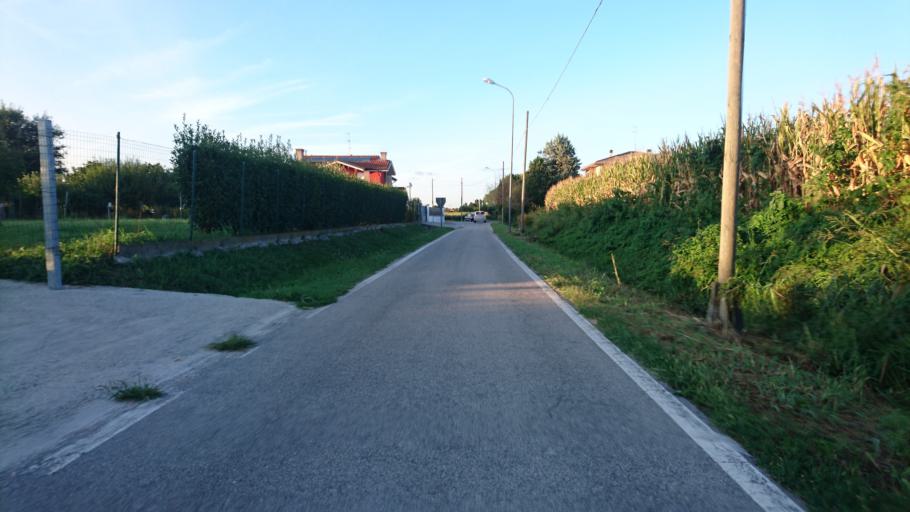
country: IT
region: Veneto
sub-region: Provincia di Padova
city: Abano Terme
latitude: 45.3469
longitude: 11.7938
